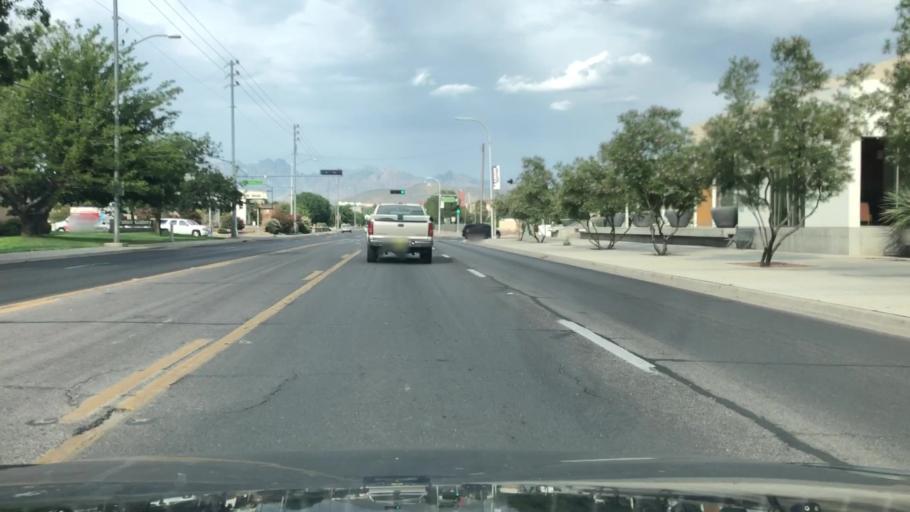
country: US
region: New Mexico
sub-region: Dona Ana County
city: University Park
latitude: 32.2828
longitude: -106.7626
